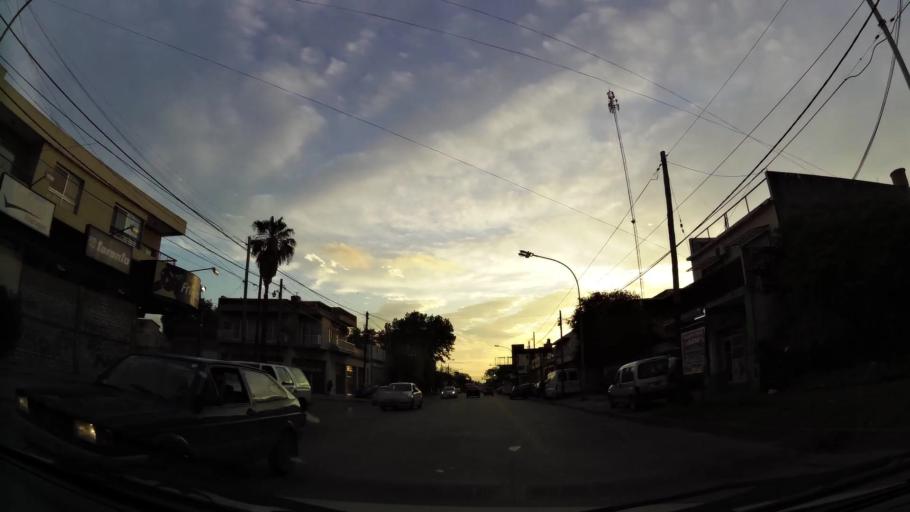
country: AR
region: Buenos Aires
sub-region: Partido de Lomas de Zamora
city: Lomas de Zamora
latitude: -34.7709
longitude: -58.3799
